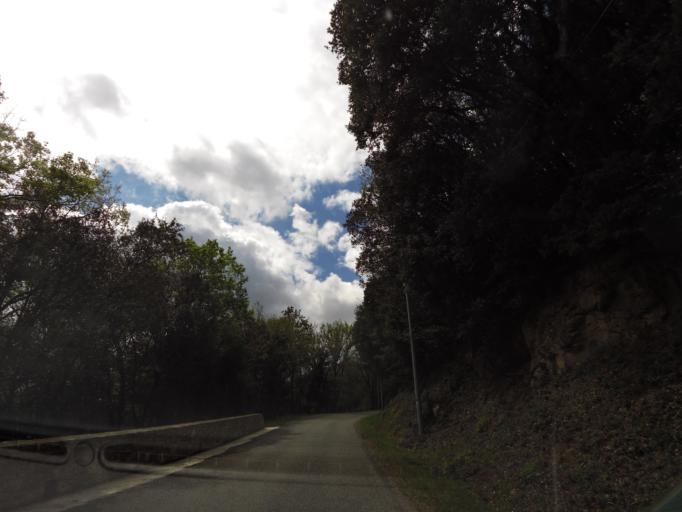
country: FR
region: Languedoc-Roussillon
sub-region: Departement de l'Aude
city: Villepinte
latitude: 43.3516
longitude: 2.1206
